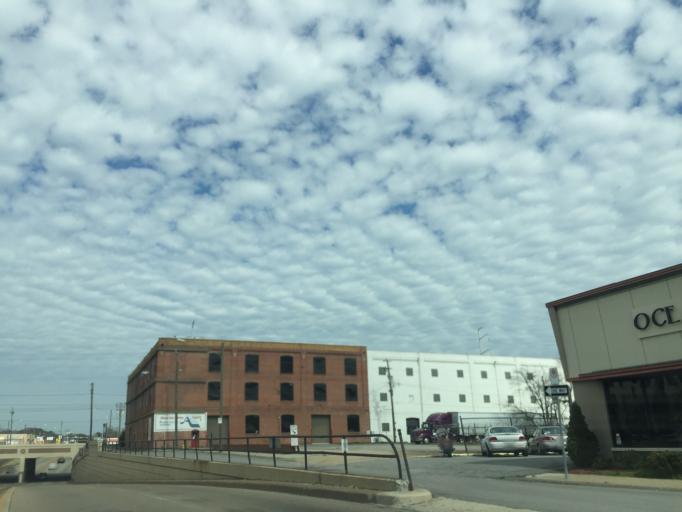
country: US
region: Virginia
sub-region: City of Norfolk
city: Norfolk
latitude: 36.8672
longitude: -76.2841
